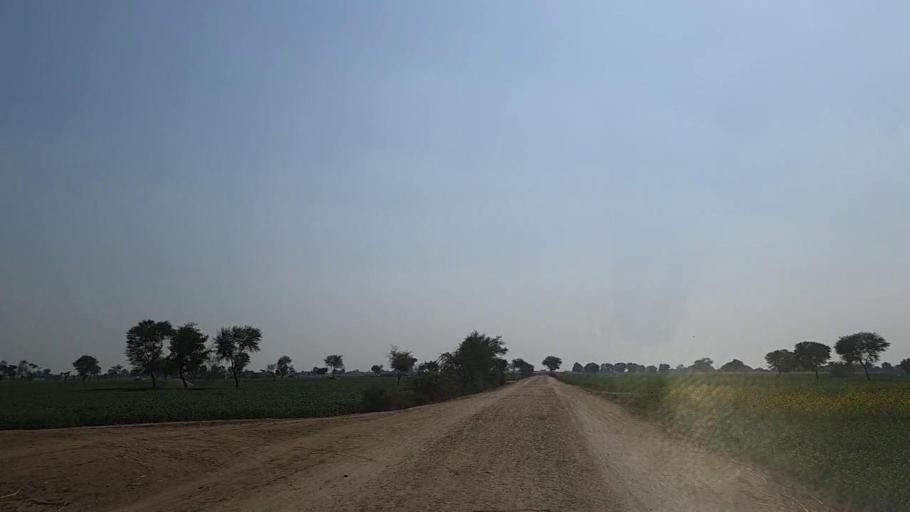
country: PK
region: Sindh
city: Daur
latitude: 26.4746
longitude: 68.2508
